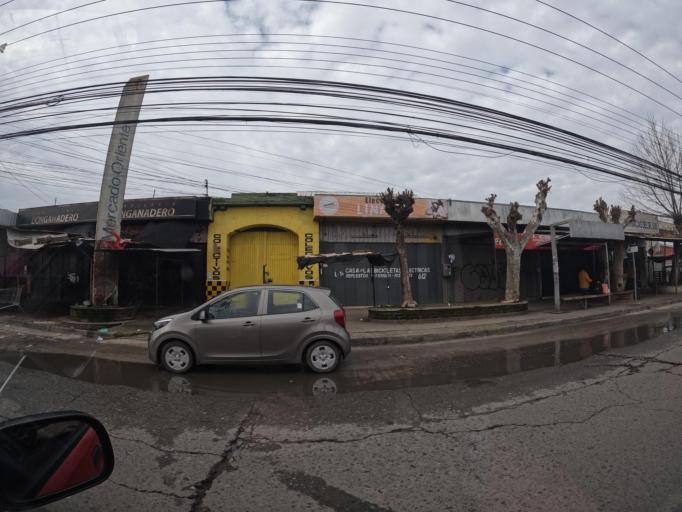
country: CL
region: Maule
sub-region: Provincia de Linares
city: Linares
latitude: -35.8461
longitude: -71.5891
